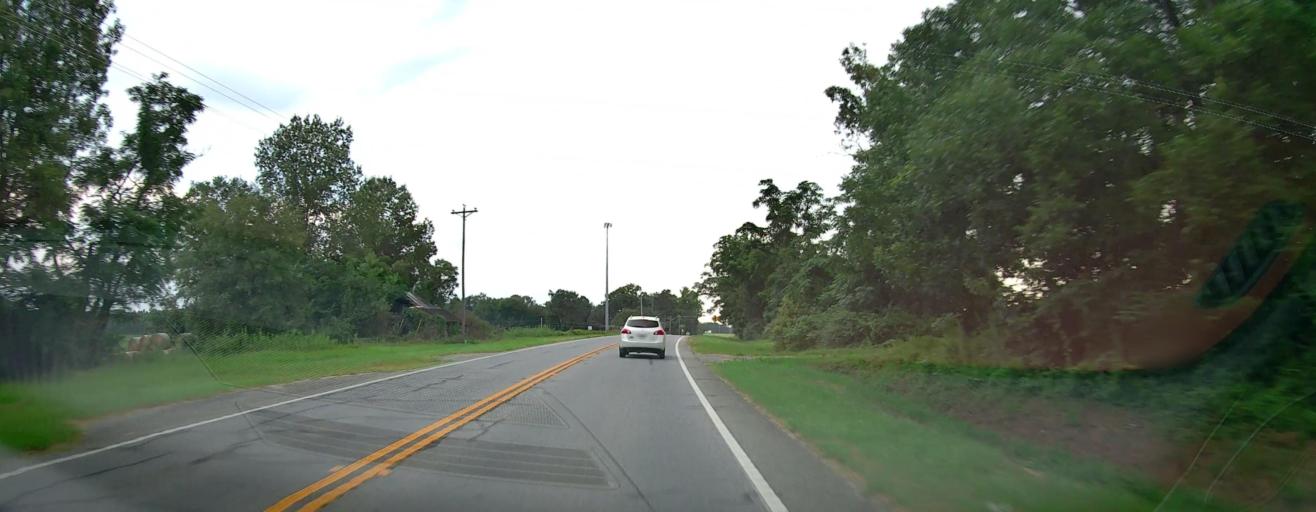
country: US
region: Georgia
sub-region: Laurens County
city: East Dublin
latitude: 32.5702
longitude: -82.8414
